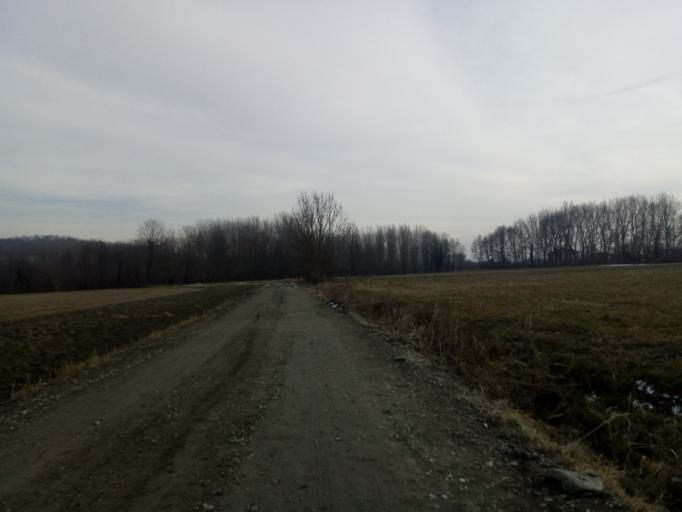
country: IT
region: Piedmont
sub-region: Provincia di Torino
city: Burolo
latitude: 45.4832
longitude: 7.9217
